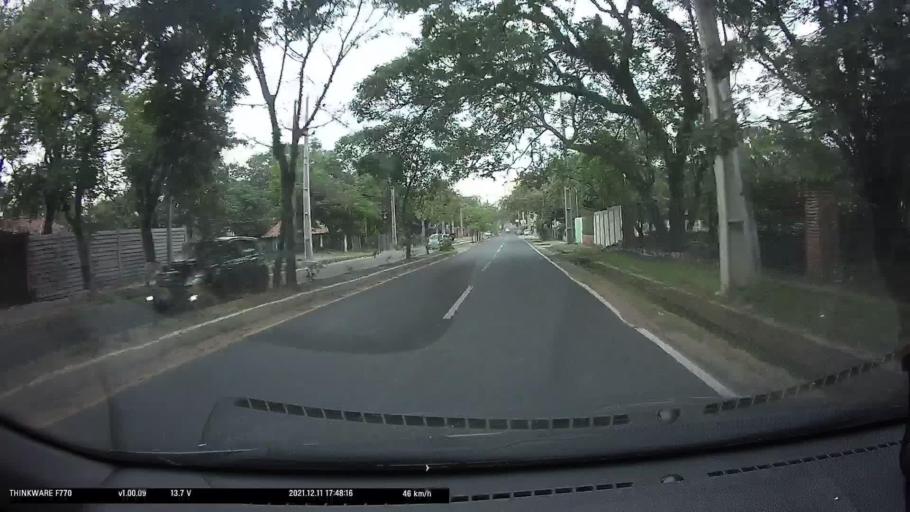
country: PY
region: Cordillera
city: San Bernardino
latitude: -25.3035
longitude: -57.2931
